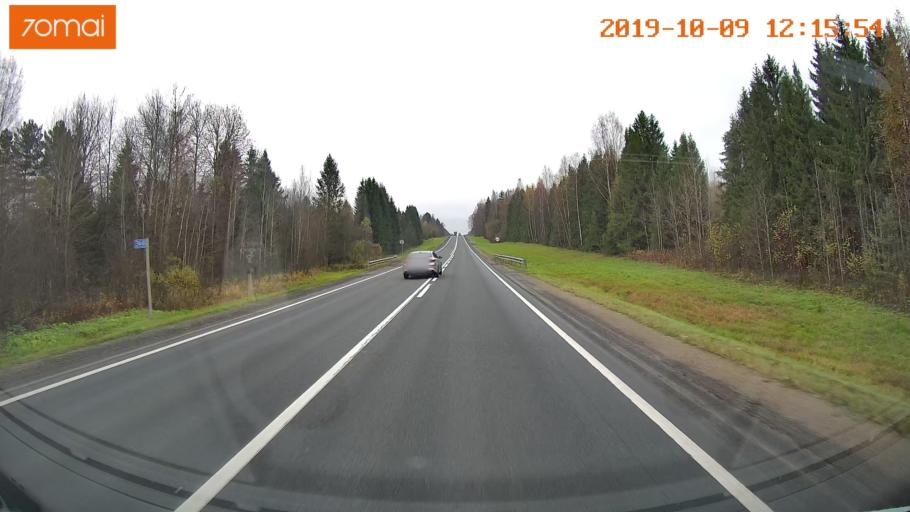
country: RU
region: Jaroslavl
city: Prechistoye
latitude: 58.4764
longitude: 40.3221
